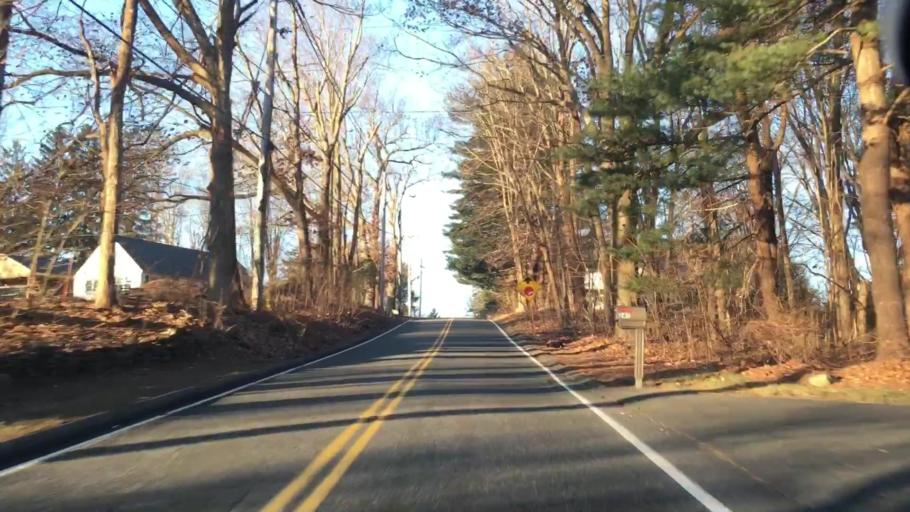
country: US
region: Massachusetts
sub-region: Hampden County
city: East Longmeadow
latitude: 42.0436
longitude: -72.4989
